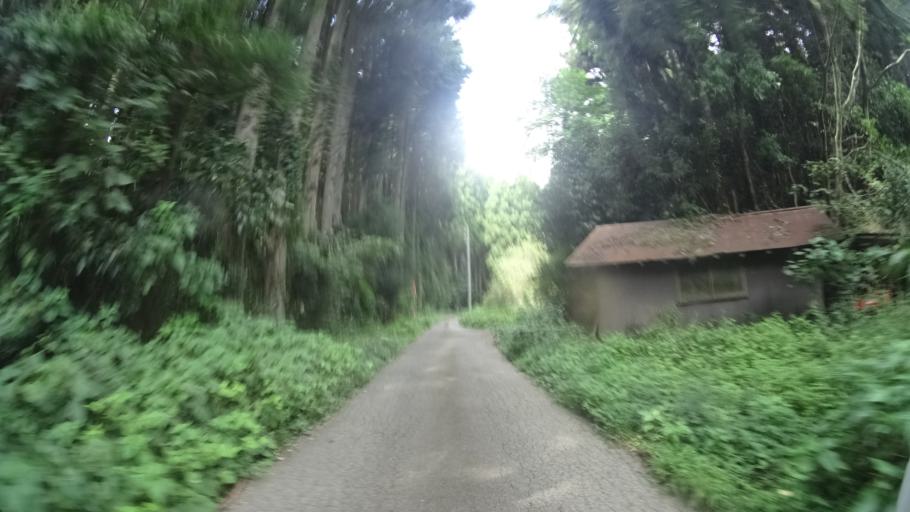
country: JP
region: Yamaguchi
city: Hagi
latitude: 34.4933
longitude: 131.5699
